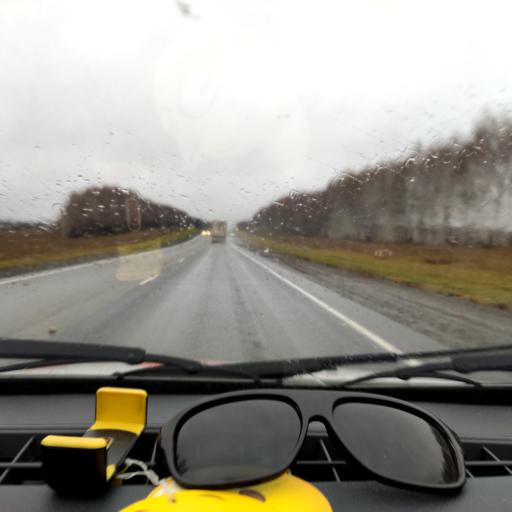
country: RU
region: Bashkortostan
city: Iglino
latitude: 54.7741
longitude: 56.4743
